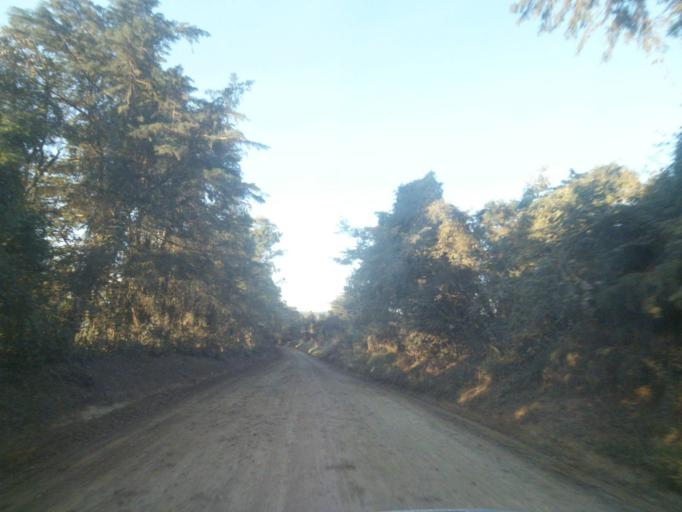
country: BR
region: Parana
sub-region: Tibagi
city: Tibagi
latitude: -24.5327
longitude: -50.5164
